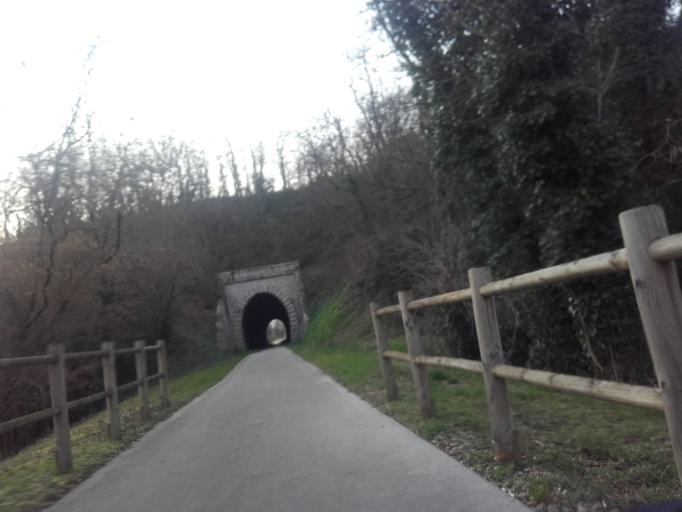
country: FR
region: Bourgogne
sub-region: Departement de la Cote-d'Or
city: Nolay
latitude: 46.9080
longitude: 4.6530
